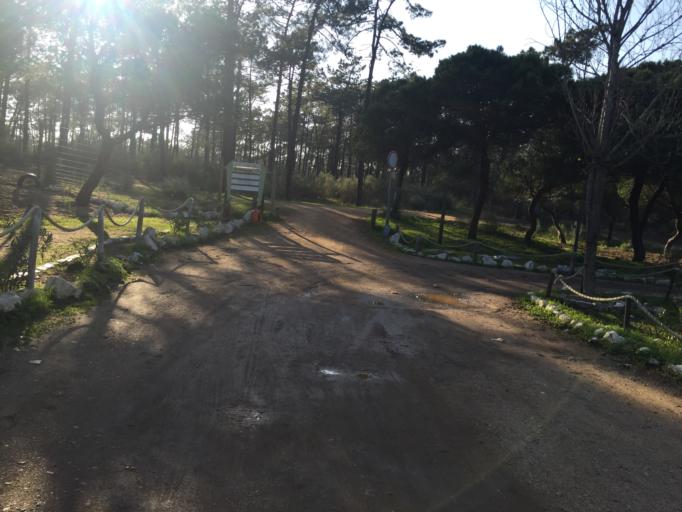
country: PT
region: Faro
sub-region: Vila Real de Santo Antonio
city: Vila Real de Santo Antonio
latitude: 37.1883
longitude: -7.4231
